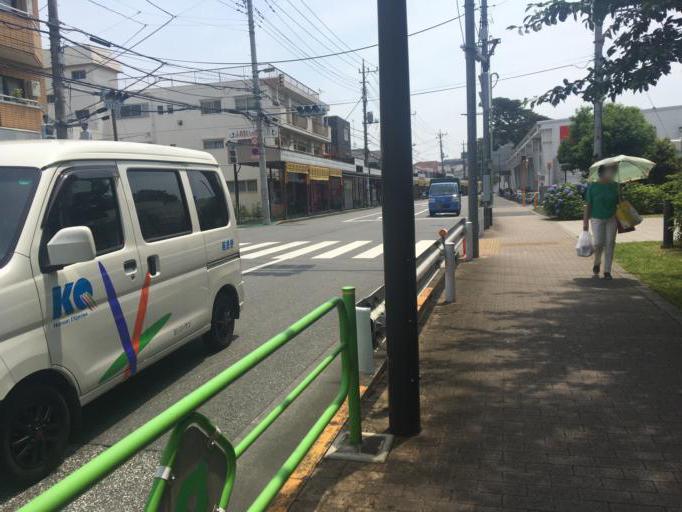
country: JP
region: Tokyo
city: Tanashicho
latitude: 35.7479
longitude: 139.5354
